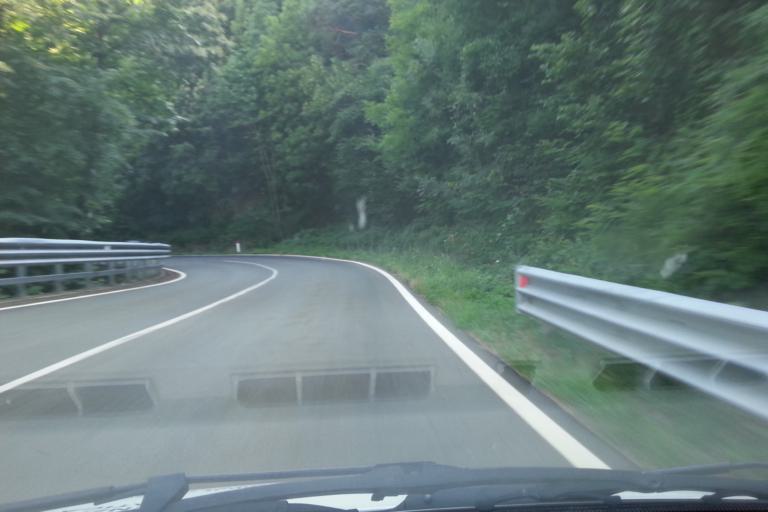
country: IT
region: Piedmont
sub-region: Provincia di Torino
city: Venaus
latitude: 45.1593
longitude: 6.9968
